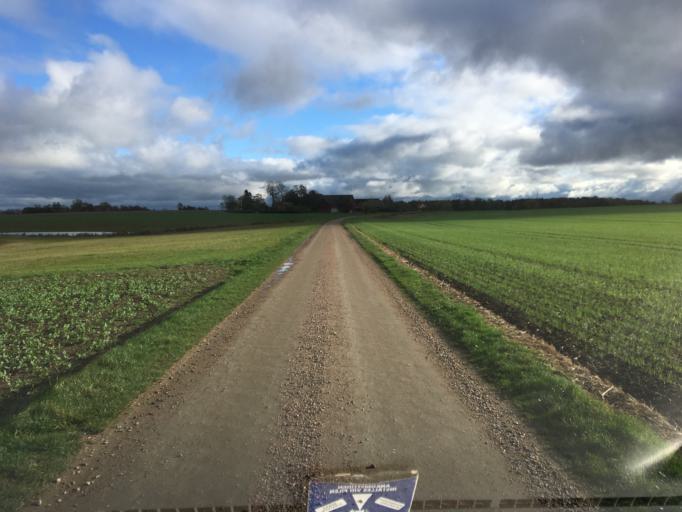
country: SE
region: Skane
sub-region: Lunds Kommun
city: Lund
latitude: 55.7404
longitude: 13.2011
